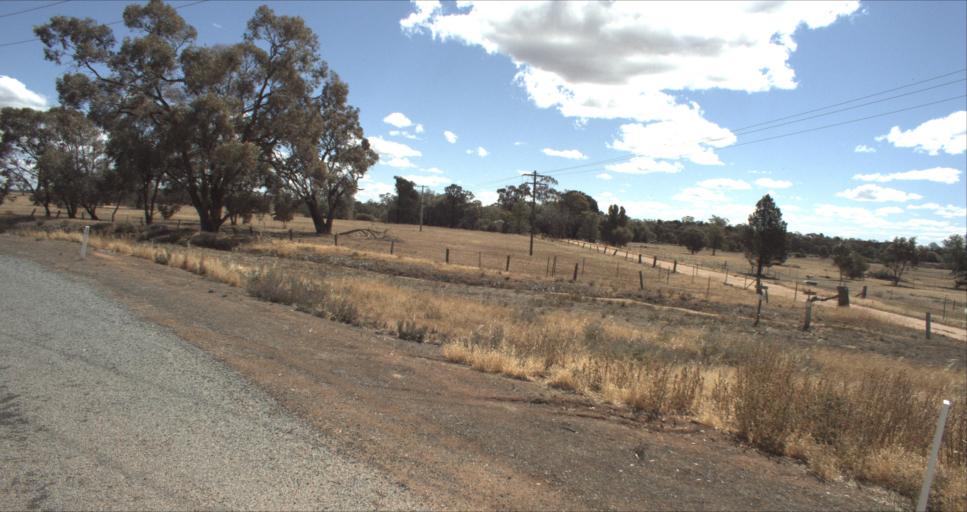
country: AU
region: New South Wales
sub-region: Leeton
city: Leeton
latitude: -34.5185
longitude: 146.2256
